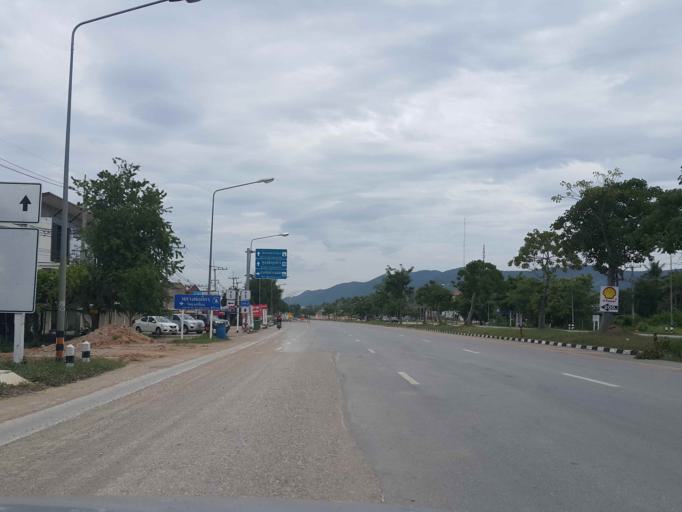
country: TH
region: Lampang
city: Thoen
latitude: 17.6272
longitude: 99.2379
